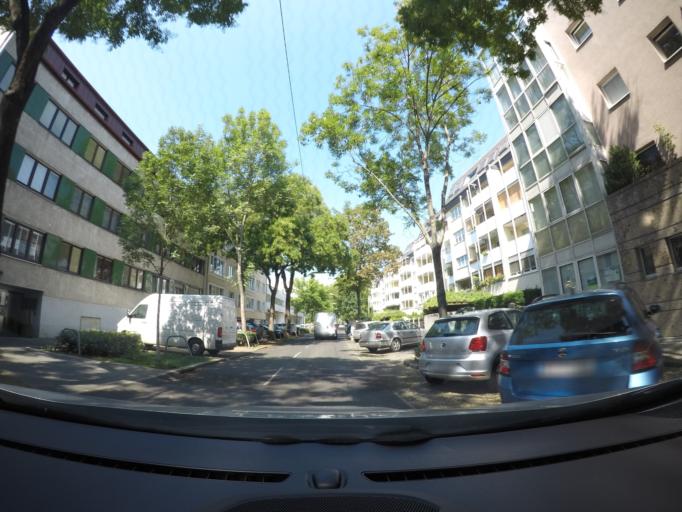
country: AT
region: Lower Austria
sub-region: Politischer Bezirk Modling
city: Perchtoldsdorf
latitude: 48.1919
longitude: 16.2682
